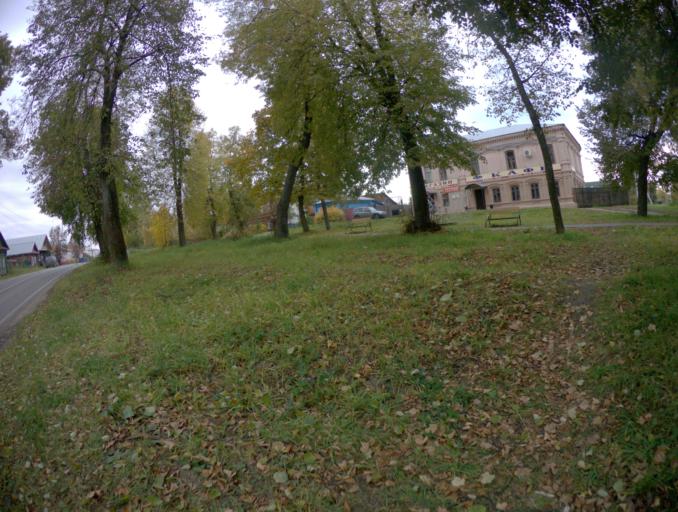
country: RU
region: Vladimir
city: Mstera
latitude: 56.3785
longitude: 41.9337
